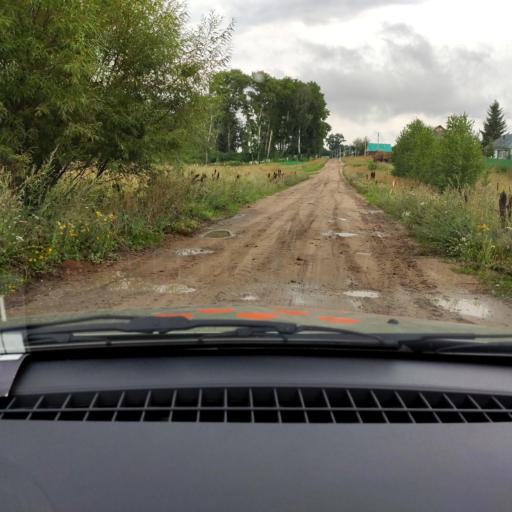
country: RU
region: Bashkortostan
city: Kabakovo
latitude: 54.5876
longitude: 56.2671
